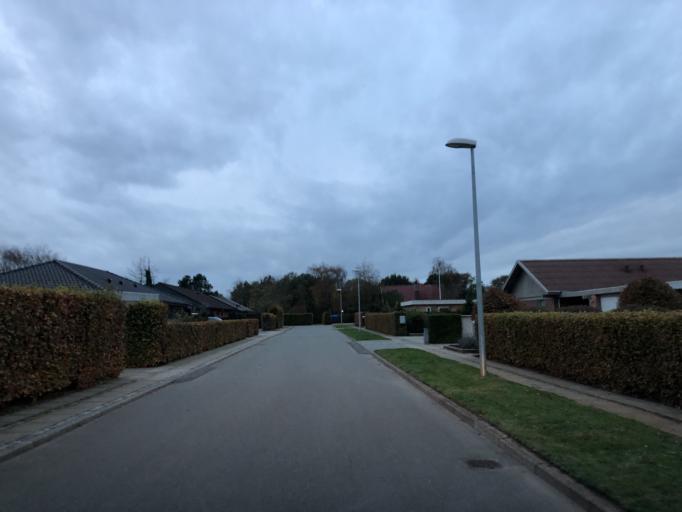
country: DK
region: Central Jutland
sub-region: Holstebro Kommune
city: Ulfborg
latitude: 56.3458
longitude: 8.3382
